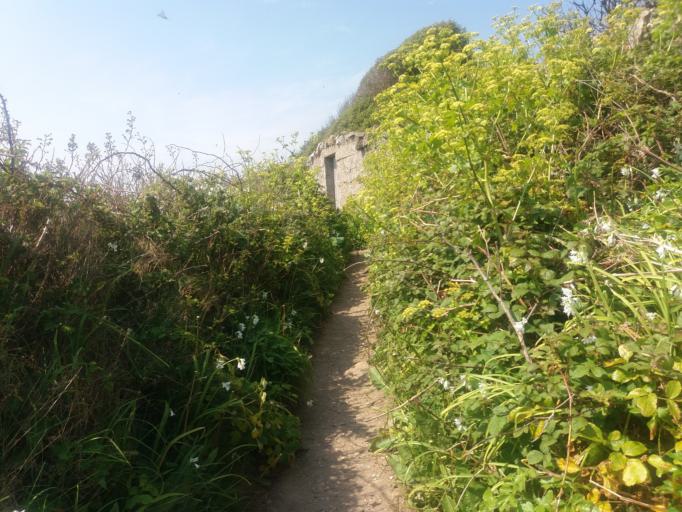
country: IE
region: Leinster
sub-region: Fingal County
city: Howth
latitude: 53.3640
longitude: -6.0855
